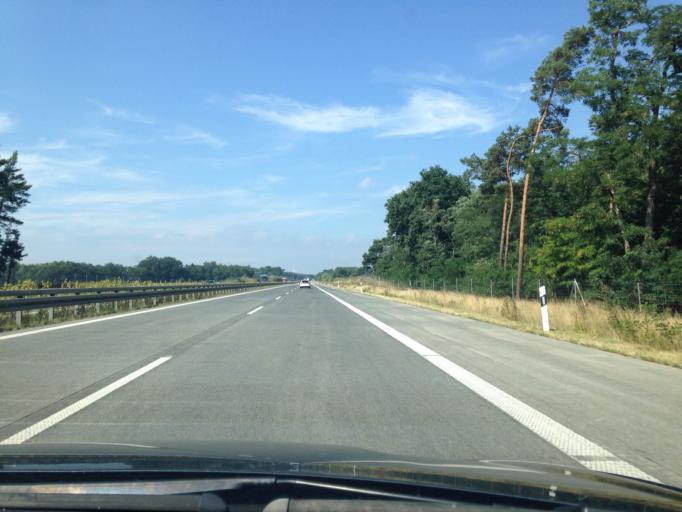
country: DE
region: Brandenburg
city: Luebben
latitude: 51.8850
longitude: 13.8571
